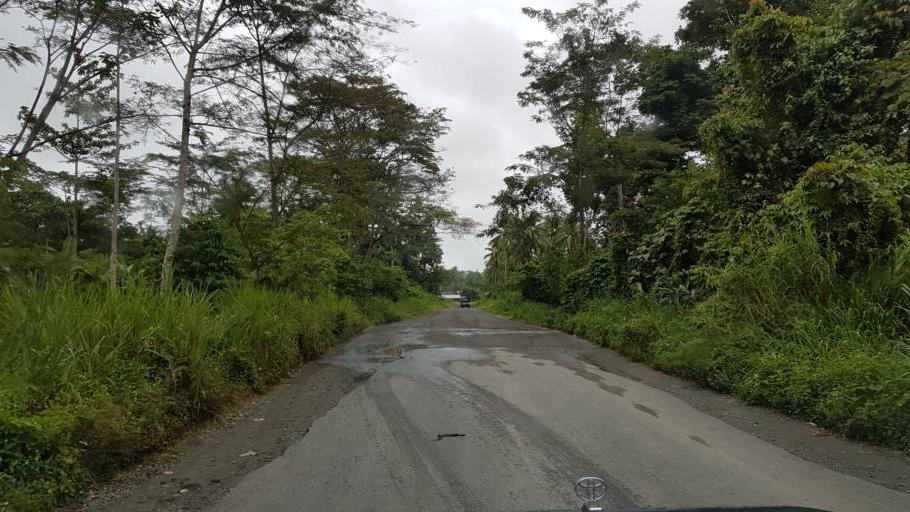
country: PG
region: Northern Province
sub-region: Sohe
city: Popondetta
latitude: -8.8258
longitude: 148.1161
